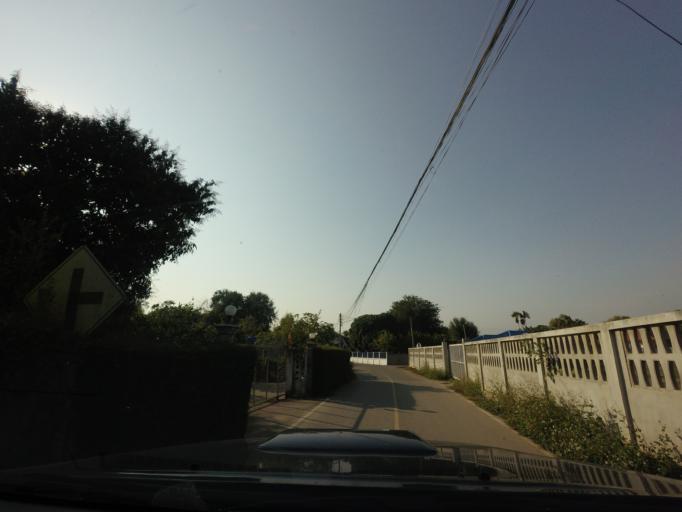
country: TH
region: Chiang Mai
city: San Sai
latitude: 18.9414
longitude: 98.9690
